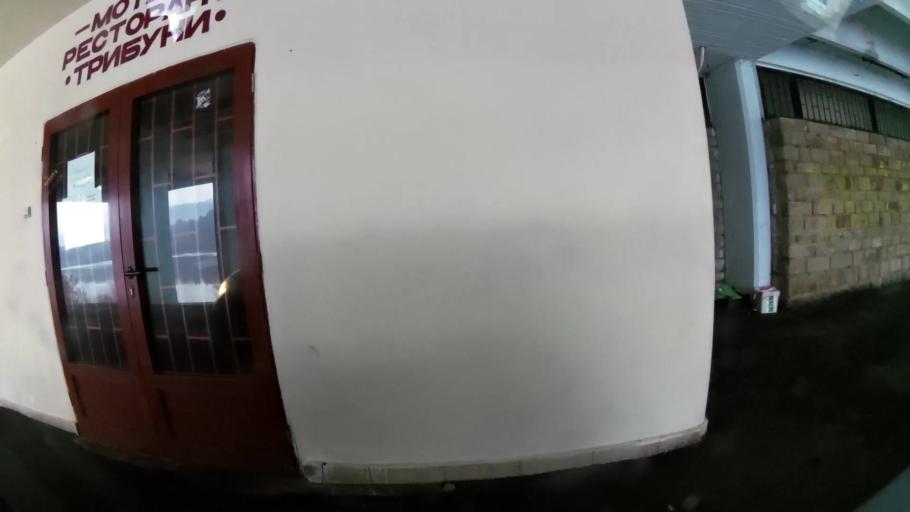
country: BG
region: Sofia-Capital
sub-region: Stolichna Obshtina
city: Sofia
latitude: 42.5926
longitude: 23.4232
